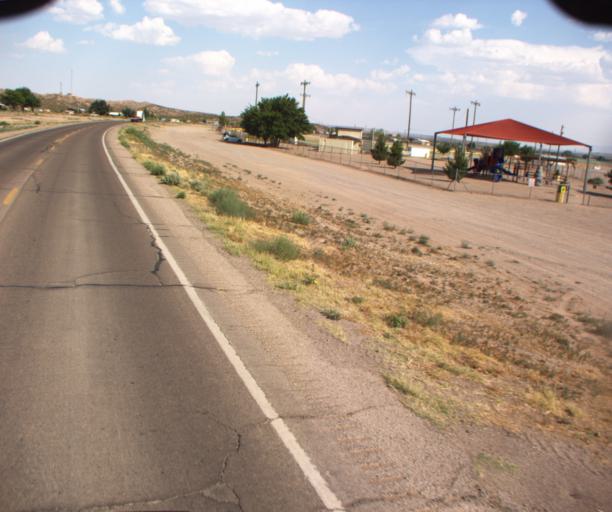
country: US
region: Arizona
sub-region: Greenlee County
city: Clifton
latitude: 32.7410
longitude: -109.0968
